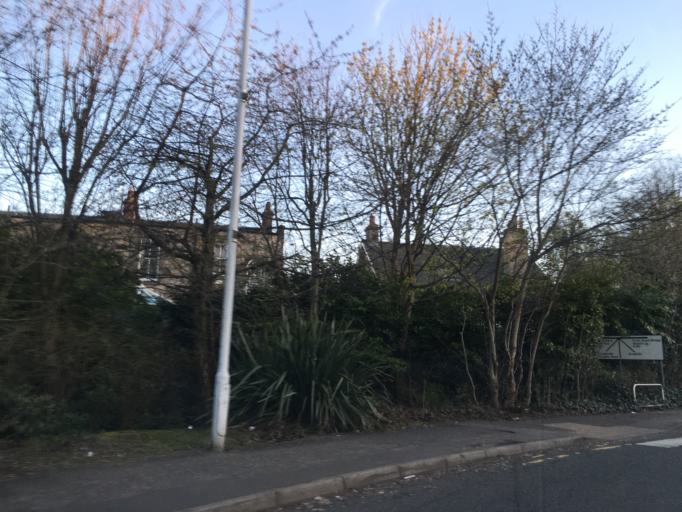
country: GB
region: Scotland
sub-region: Edinburgh
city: Edinburgh
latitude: 55.9568
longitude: -3.2414
